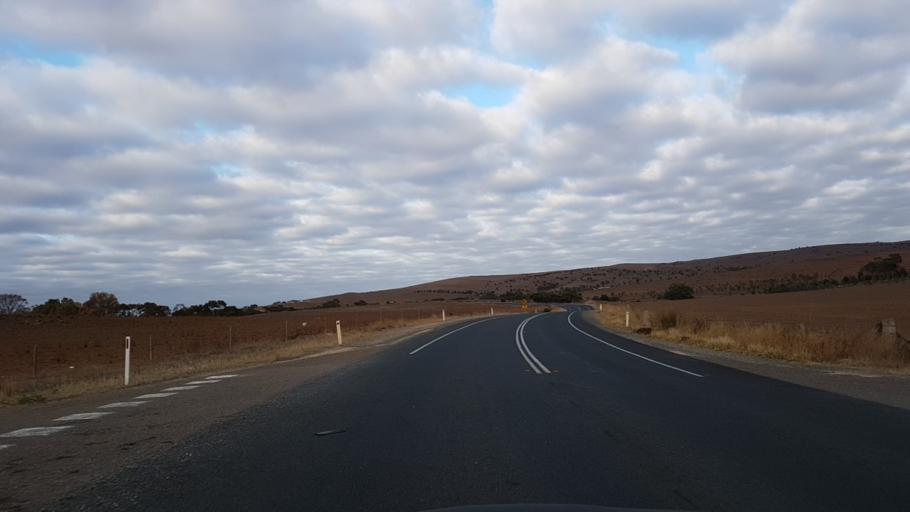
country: AU
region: South Australia
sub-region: Mount Barker
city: Callington
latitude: -35.1335
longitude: 139.0328
